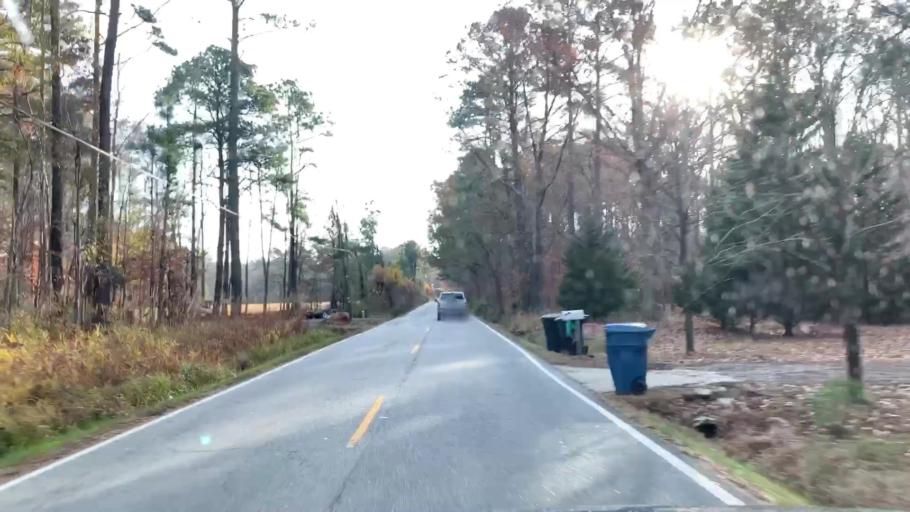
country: US
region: Virginia
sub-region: City of Virginia Beach
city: Virginia Beach
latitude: 36.7384
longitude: -76.1057
